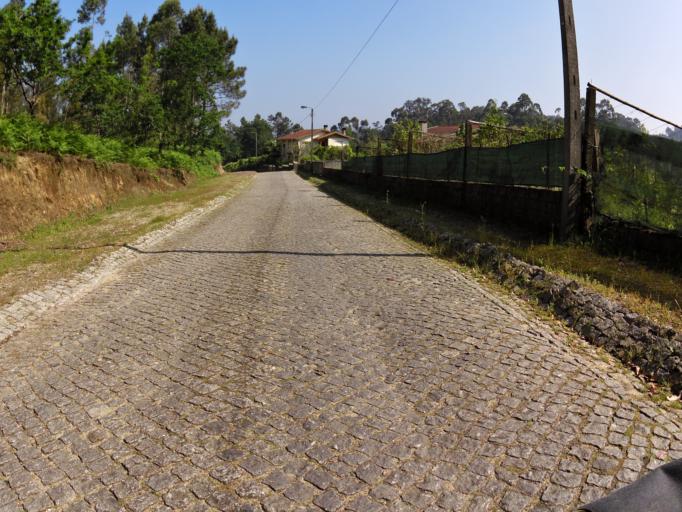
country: PT
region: Porto
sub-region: Vila Nova de Gaia
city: Olival
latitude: 41.0430
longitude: -8.5354
